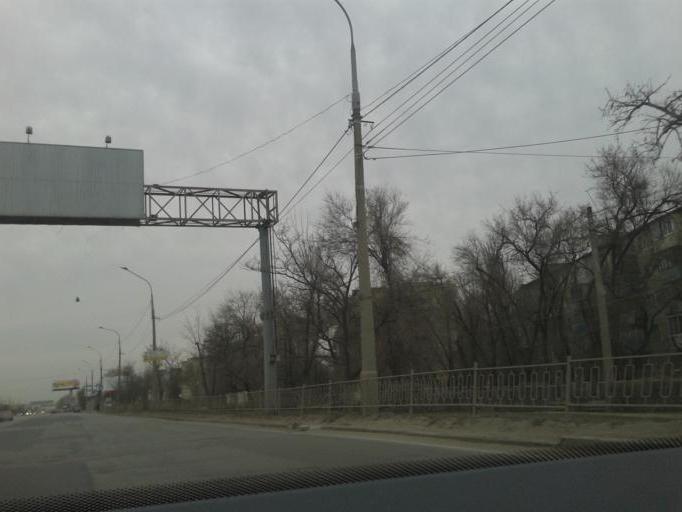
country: RU
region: Volgograd
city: Volgograd
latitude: 48.7565
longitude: 44.4804
